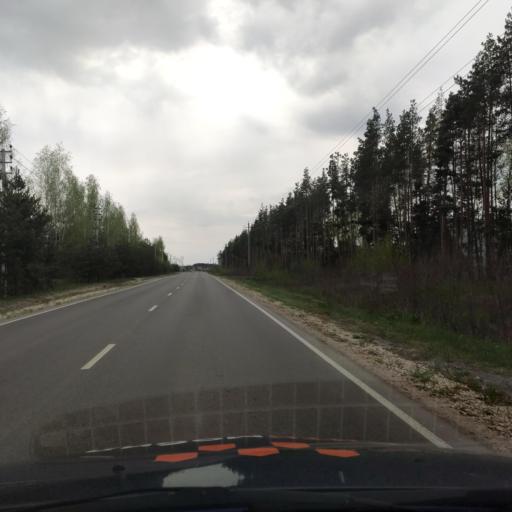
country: RU
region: Voronezj
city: Podgornoye
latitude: 51.8615
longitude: 39.1663
